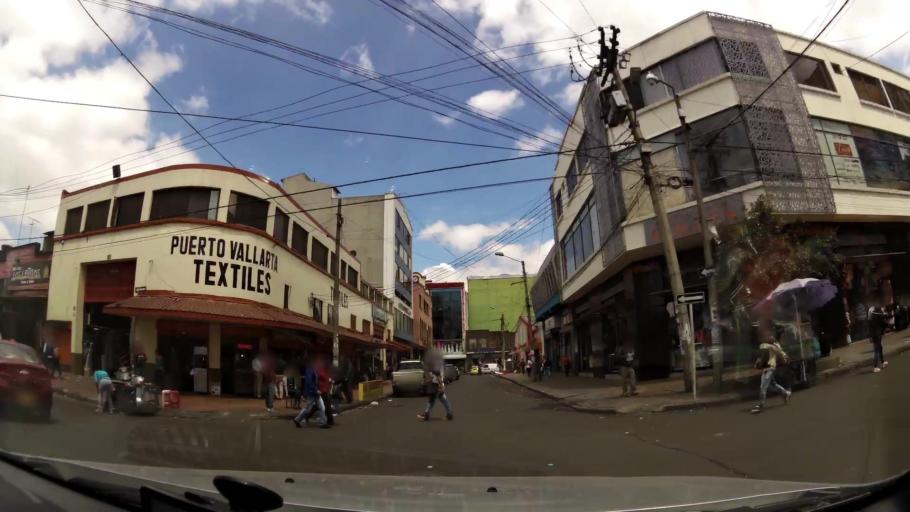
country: CO
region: Bogota D.C.
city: Bogota
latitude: 4.6035
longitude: -74.0883
